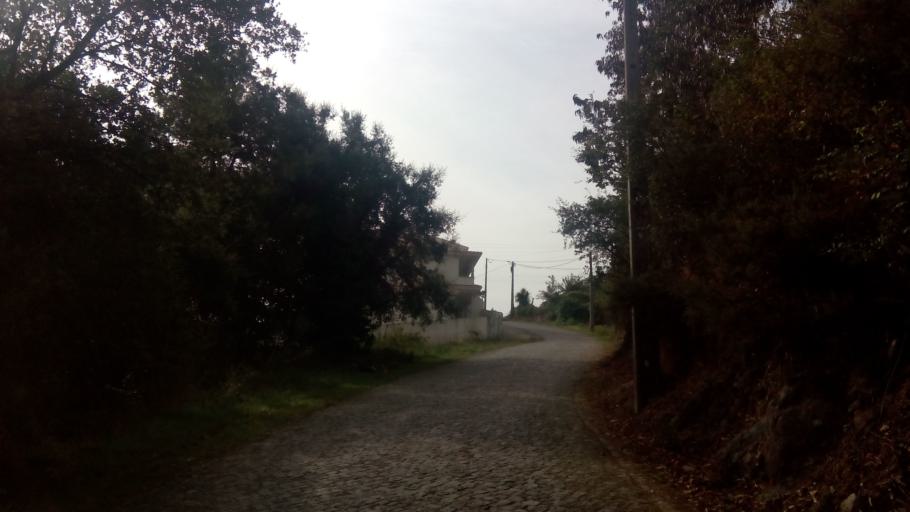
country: PT
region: Porto
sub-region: Paredes
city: Gandra
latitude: 41.1846
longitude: -8.4356
